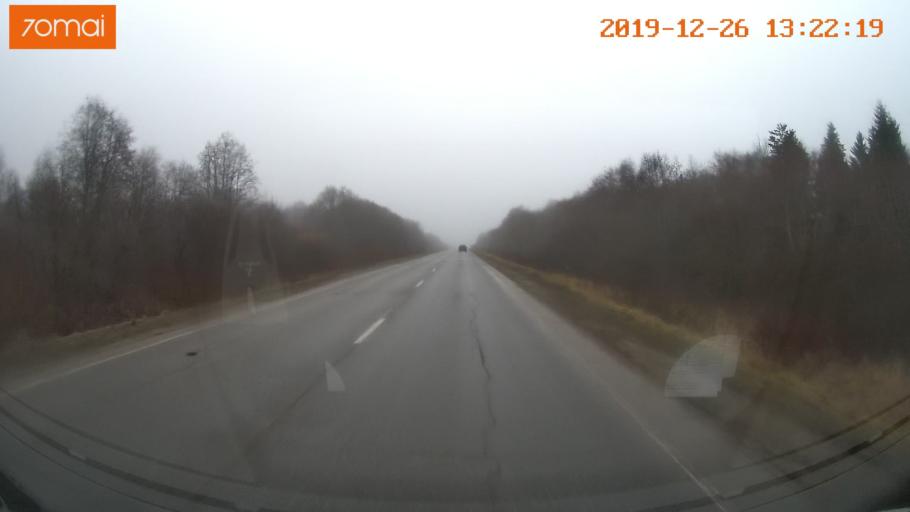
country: RU
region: Vologda
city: Cherepovets
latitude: 58.9032
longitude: 38.1703
